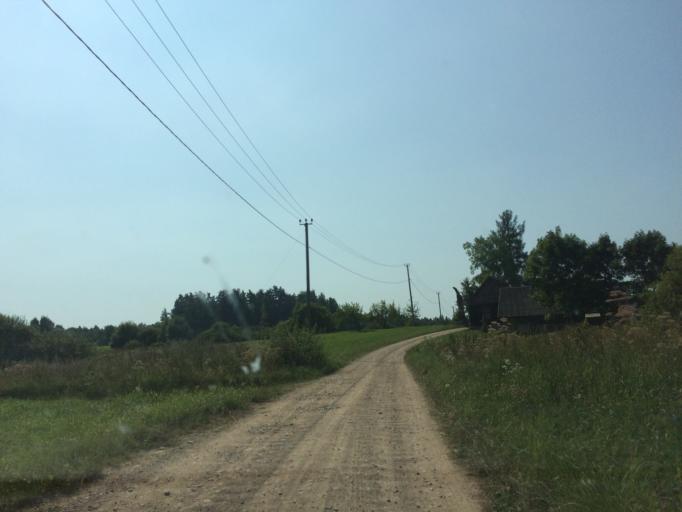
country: LV
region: Ludzas Rajons
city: Ludza
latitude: 56.5425
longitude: 27.5856
